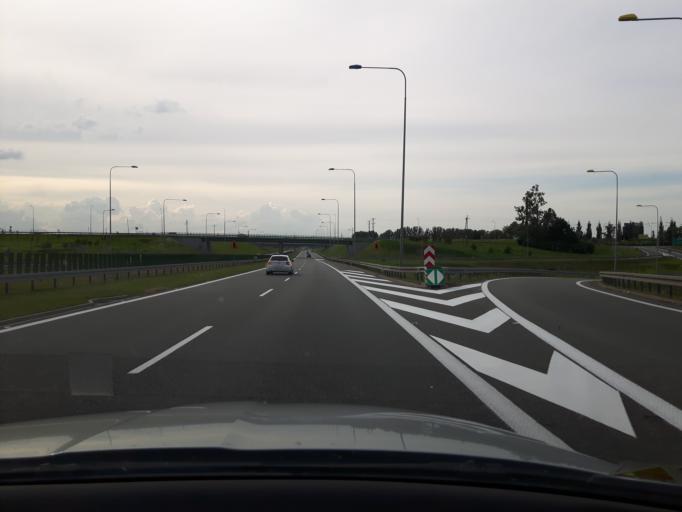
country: PL
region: Warmian-Masurian Voivodeship
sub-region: Powiat elblaski
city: Paslek
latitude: 54.0408
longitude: 19.6657
